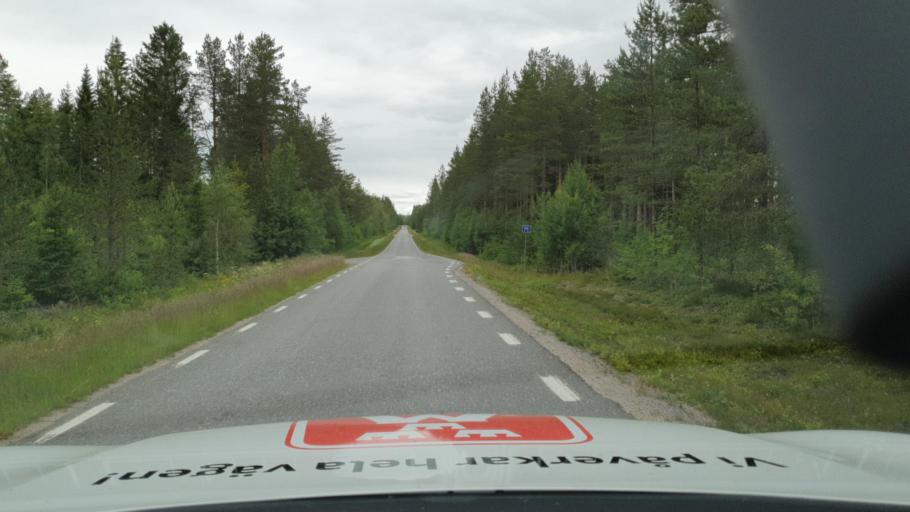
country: SE
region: Vaesterbotten
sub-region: Nordmalings Kommun
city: Nordmaling
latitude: 63.4890
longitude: 19.4392
